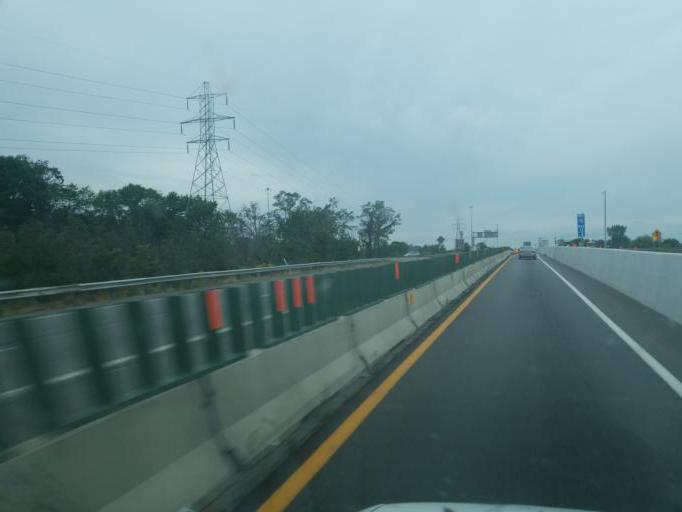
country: US
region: Ohio
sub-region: Summit County
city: Norton
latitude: 41.0400
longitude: -81.6601
